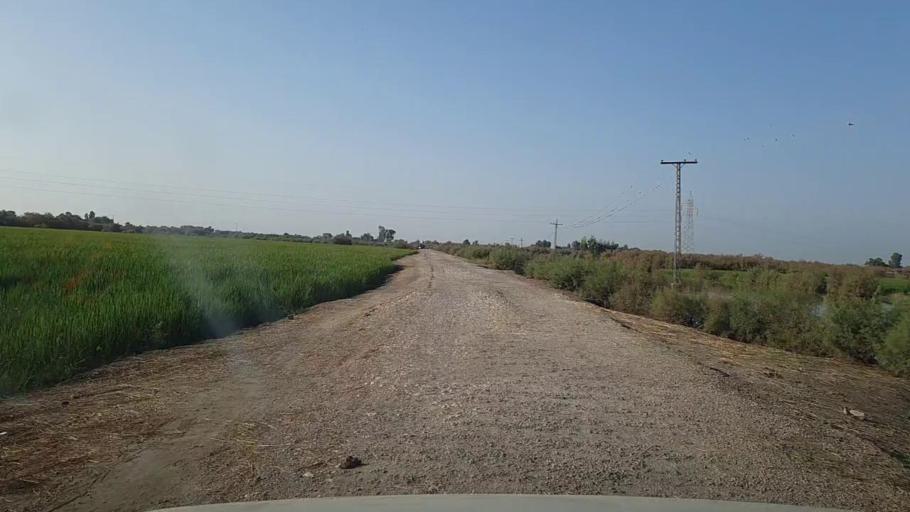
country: PK
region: Sindh
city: Kandhkot
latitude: 28.3070
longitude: 69.3285
